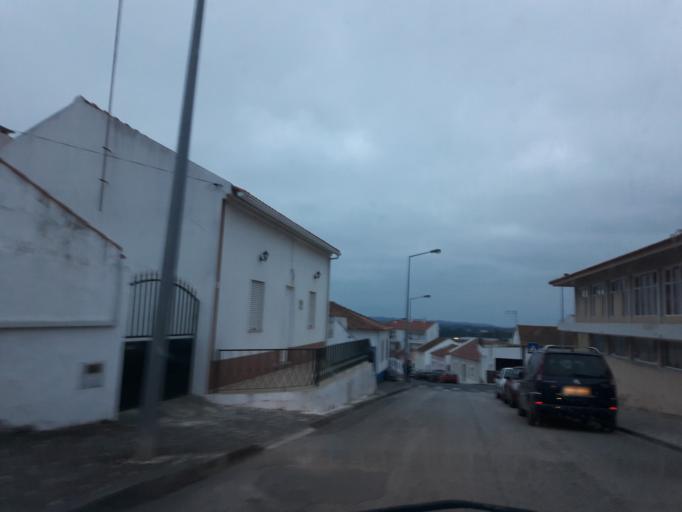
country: PT
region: Leiria
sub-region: Obidos
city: Obidos
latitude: 39.3727
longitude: -9.1294
